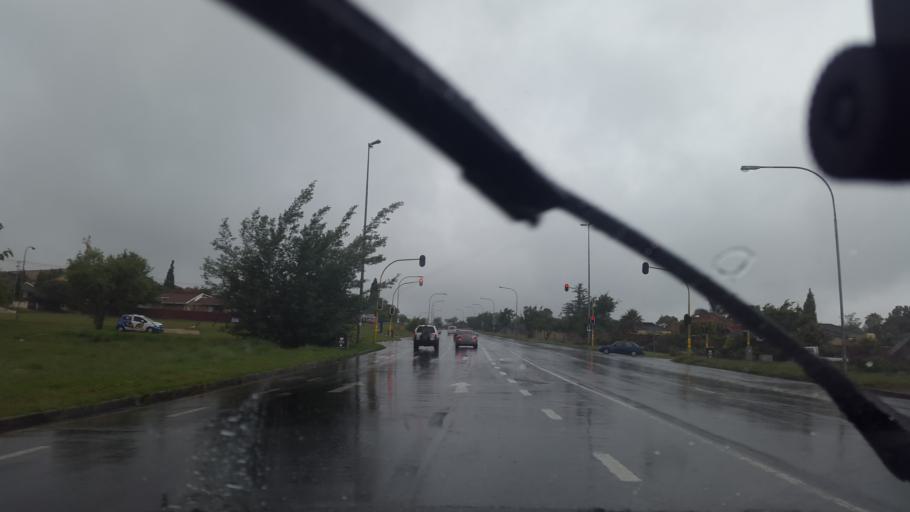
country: ZA
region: Gauteng
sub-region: City of Johannesburg Metropolitan Municipality
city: Johannesburg
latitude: -26.2741
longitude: 28.0245
